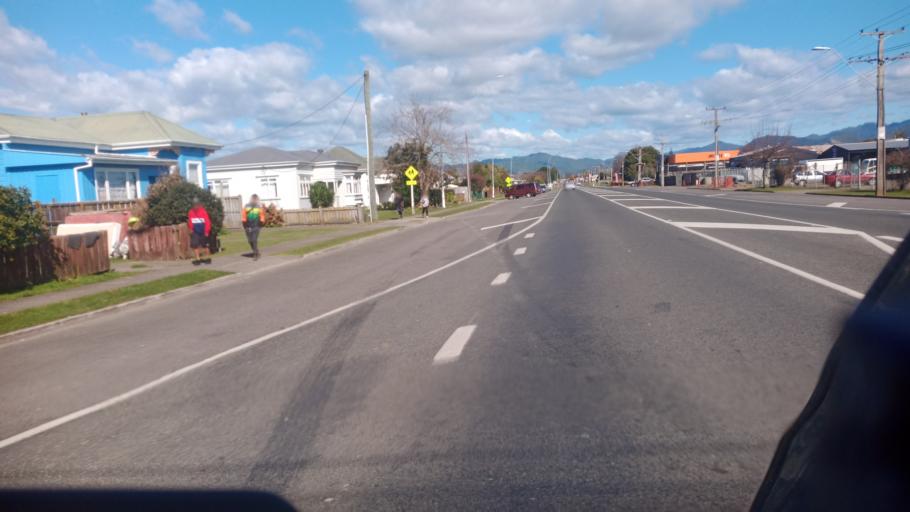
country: NZ
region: Bay of Plenty
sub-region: Opotiki District
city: Opotiki
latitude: -38.0064
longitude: 177.2871
